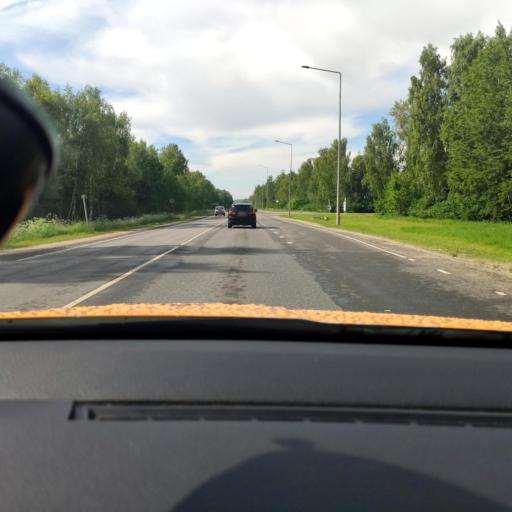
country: RU
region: Moskovskaya
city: Stupino
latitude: 54.9308
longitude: 38.0449
